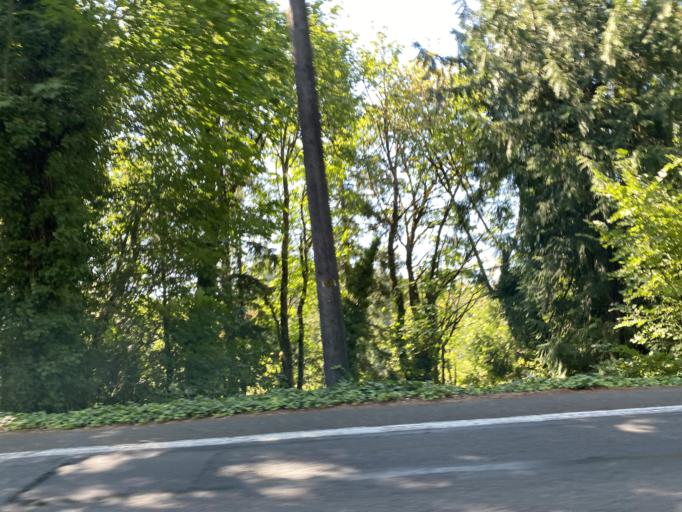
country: US
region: Washington
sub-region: Thurston County
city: Olympia
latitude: 47.0296
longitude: -122.8843
